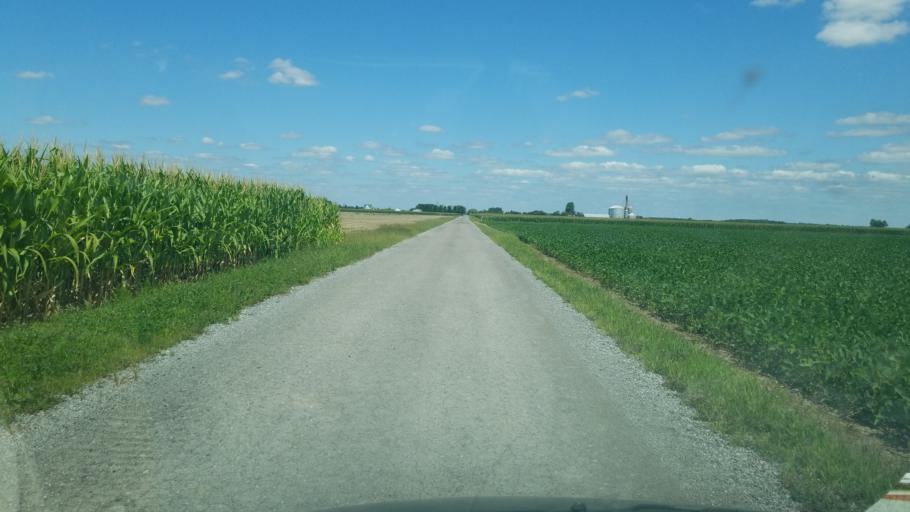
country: US
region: Ohio
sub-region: Fulton County
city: Delta
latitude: 41.6761
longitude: -84.0166
